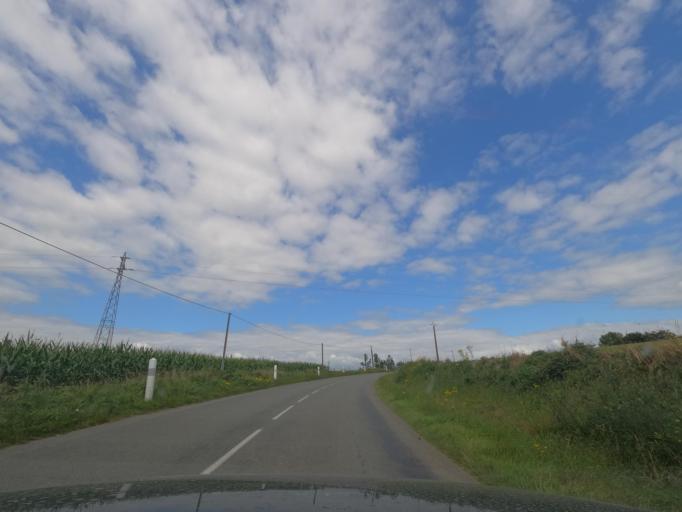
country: FR
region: Pays de la Loire
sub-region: Departement de la Mayenne
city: Landivy
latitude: 48.4562
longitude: -1.0624
